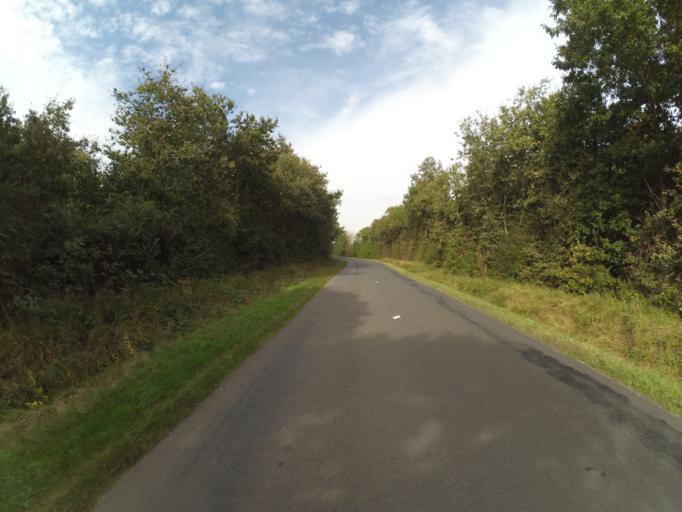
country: FR
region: Pays de la Loire
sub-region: Departement de Maine-et-Loire
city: Saint-Jean
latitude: 47.1941
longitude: -0.3533
